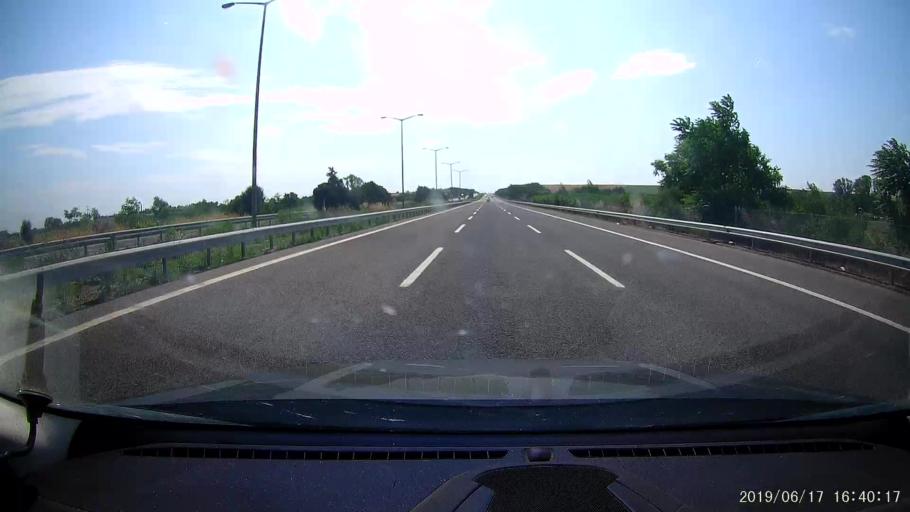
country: TR
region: Kirklareli
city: Luleburgaz
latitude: 41.4498
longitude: 27.3832
